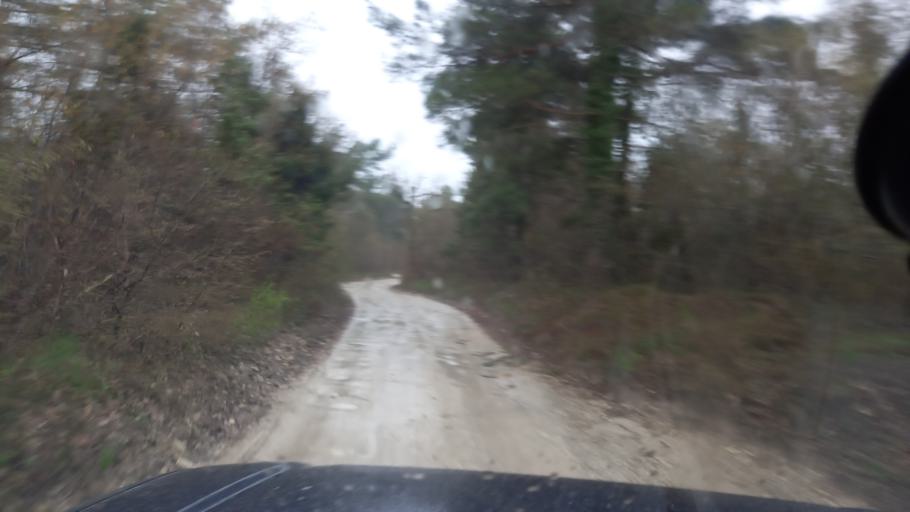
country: RU
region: Krasnodarskiy
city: Dzhubga
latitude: 44.3204
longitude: 38.6879
